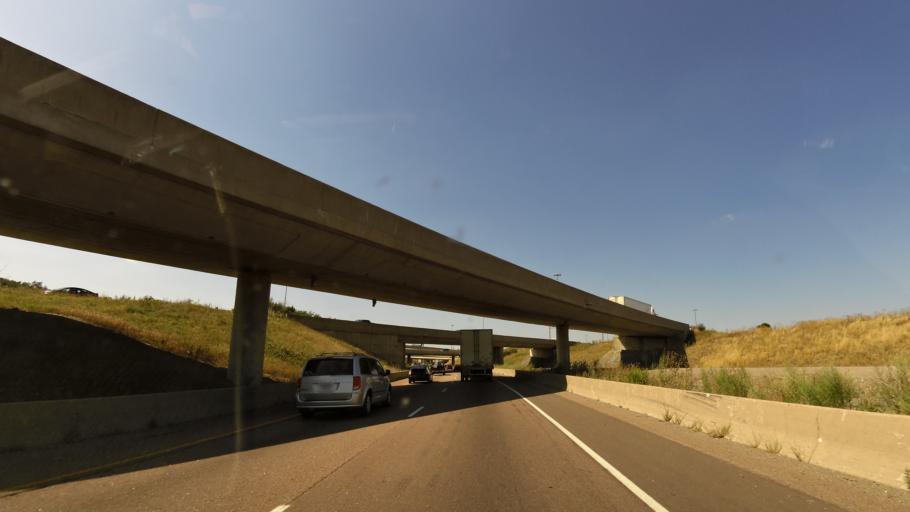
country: CA
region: Ontario
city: Mississauga
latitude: 43.6360
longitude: -79.6538
